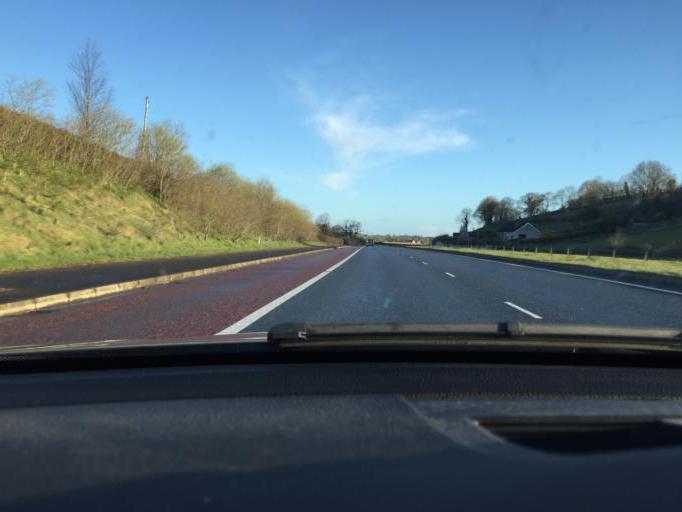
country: GB
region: Northern Ireland
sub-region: Newry and Mourne District
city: Newry
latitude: 54.2412
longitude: -6.3216
